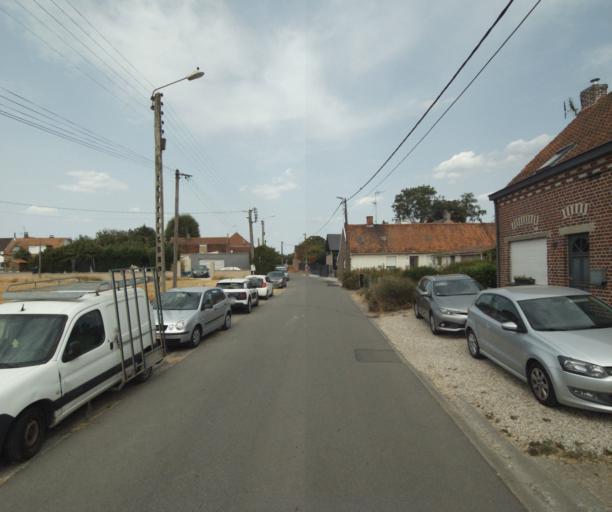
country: BE
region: Wallonia
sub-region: Province du Hainaut
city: Estaimpuis
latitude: 50.7005
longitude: 3.2608
